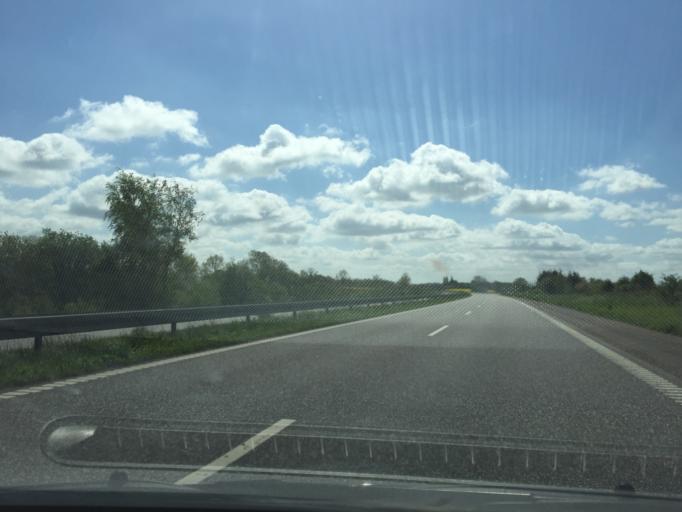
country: DK
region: Zealand
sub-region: Guldborgsund Kommune
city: Norre Alslev
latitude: 54.8621
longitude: 11.8520
